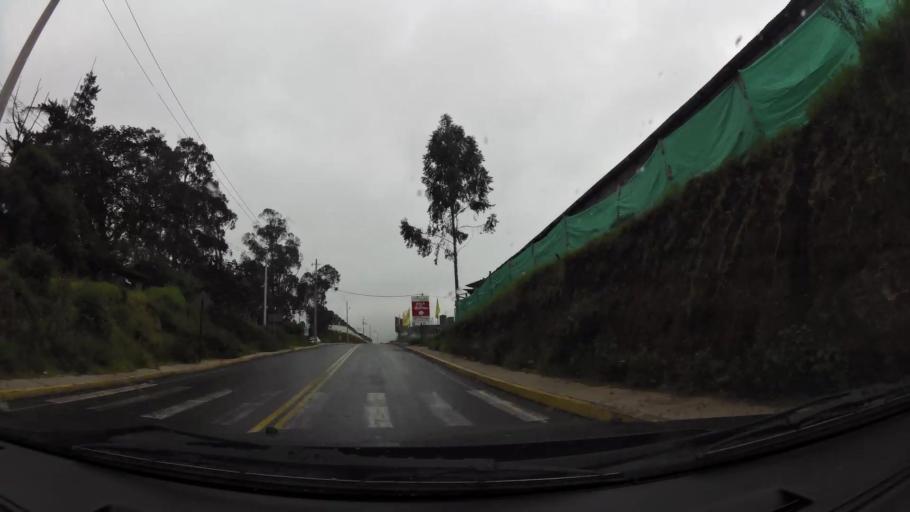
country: EC
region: Pichincha
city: Sangolqui
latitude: -0.2715
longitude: -78.4540
